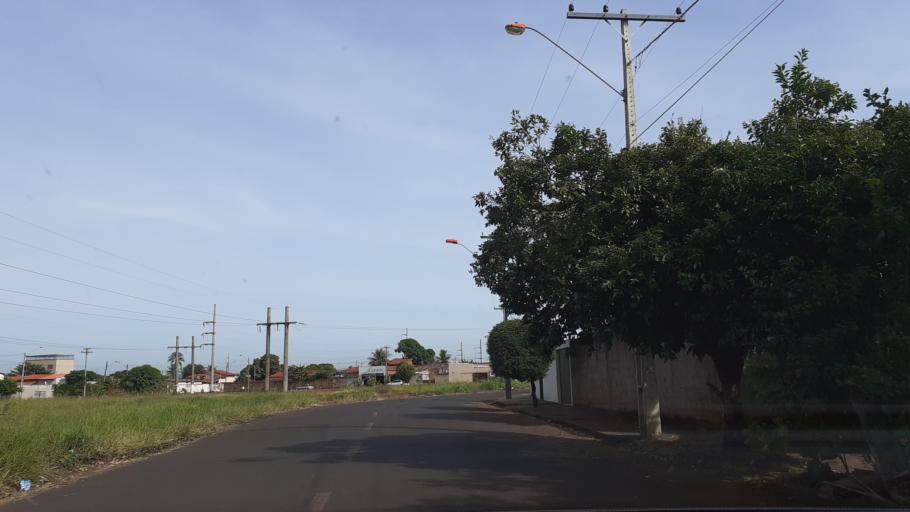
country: BR
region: Goias
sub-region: Itumbiara
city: Itumbiara
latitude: -18.4194
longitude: -49.2444
